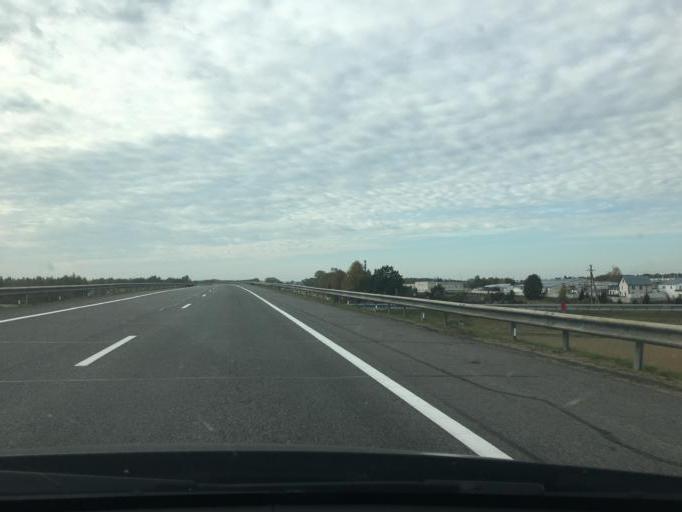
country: BY
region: Minsk
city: Dzyarzhynsk
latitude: 53.6783
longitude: 27.1926
